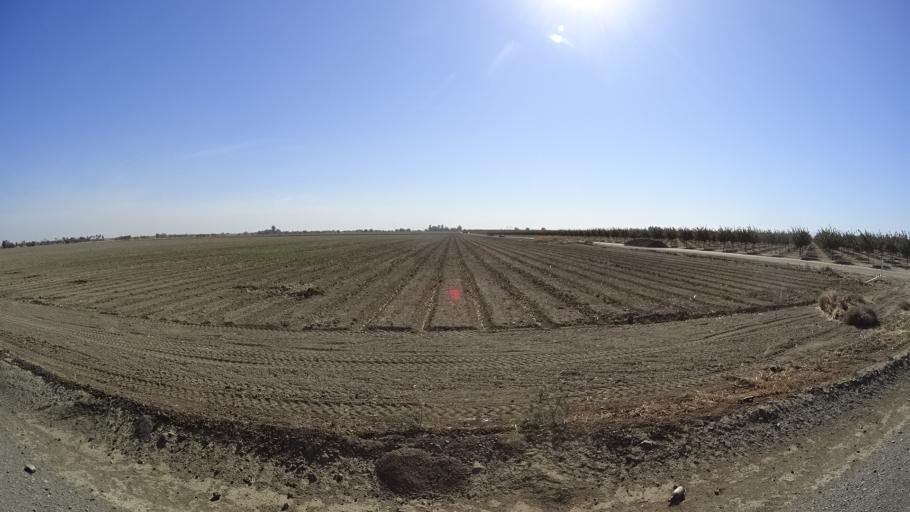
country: US
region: California
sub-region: Yolo County
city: Woodland
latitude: 38.6411
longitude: -121.7753
